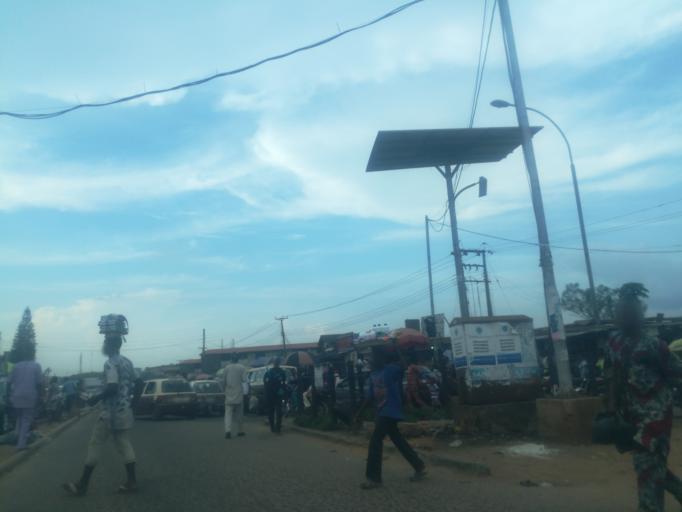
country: NG
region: Oyo
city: Ibadan
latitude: 7.4234
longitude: 3.8984
